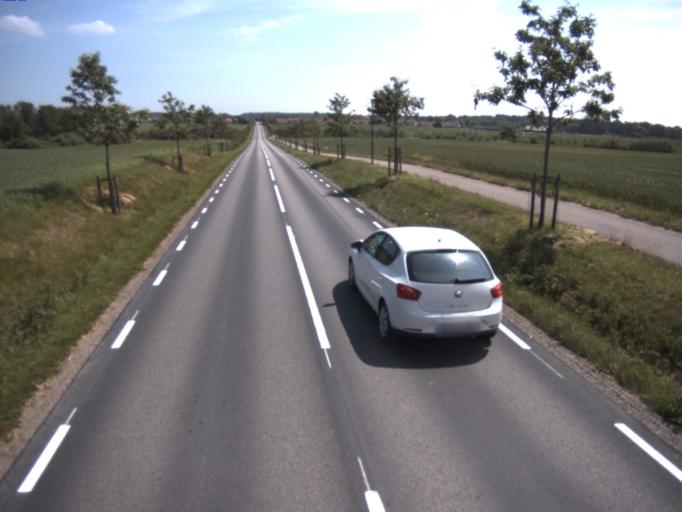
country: DK
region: Capital Region
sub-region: Helsingor Kommune
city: Helsingor
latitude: 56.1035
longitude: 12.6434
